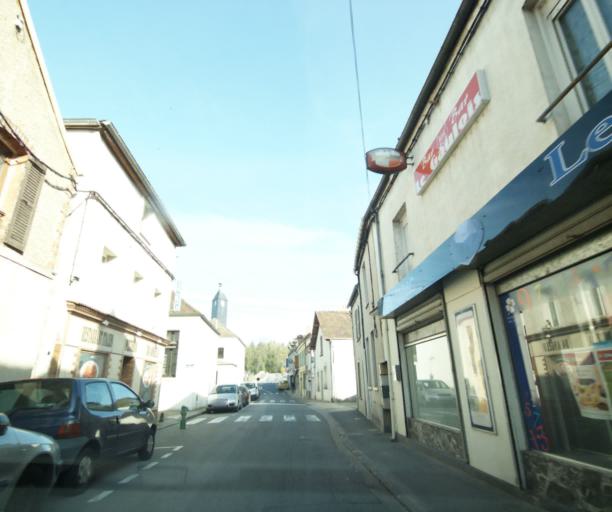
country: FR
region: Ile-de-France
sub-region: Departement de Seine-et-Marne
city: Saint-Mammes
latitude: 48.3885
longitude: 2.8086
